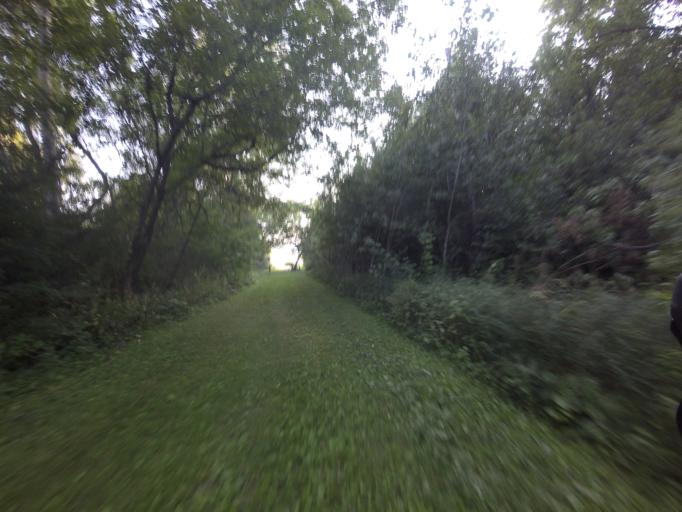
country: CA
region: Ontario
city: Bells Corners
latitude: 45.3140
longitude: -75.7374
